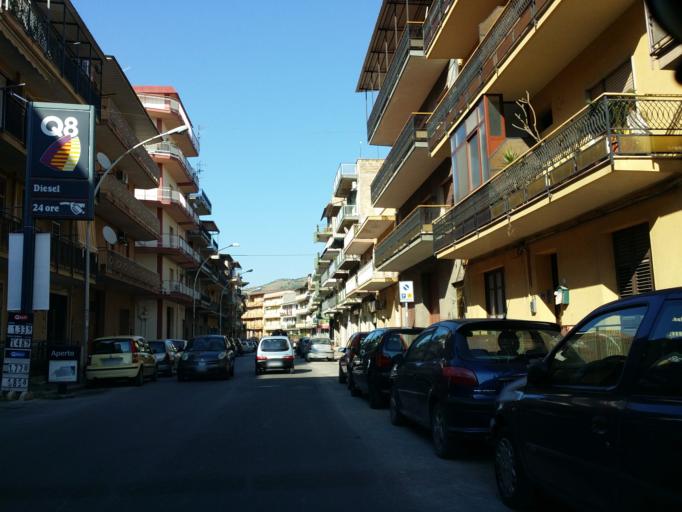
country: IT
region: Sicily
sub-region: Palermo
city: Misilmeri
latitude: 38.0333
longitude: 13.4532
